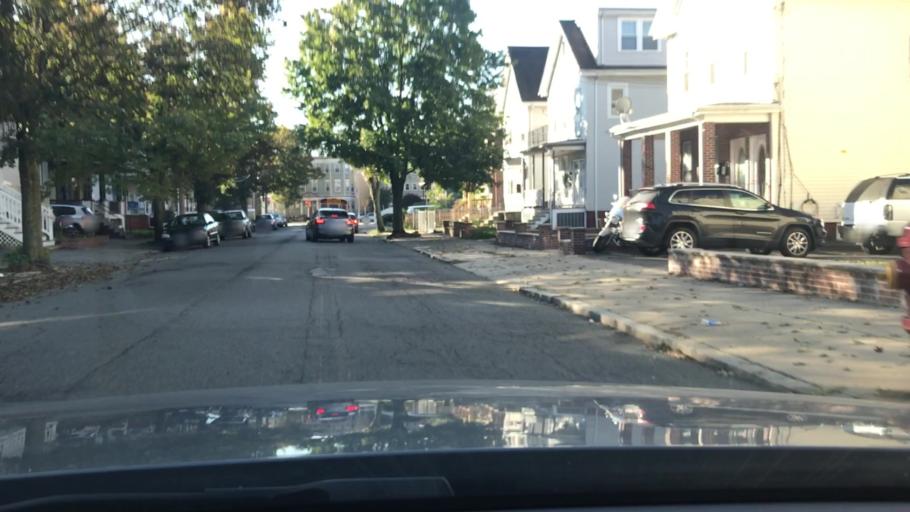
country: US
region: Massachusetts
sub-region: Middlesex County
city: Malden
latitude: 42.4304
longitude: -71.0621
